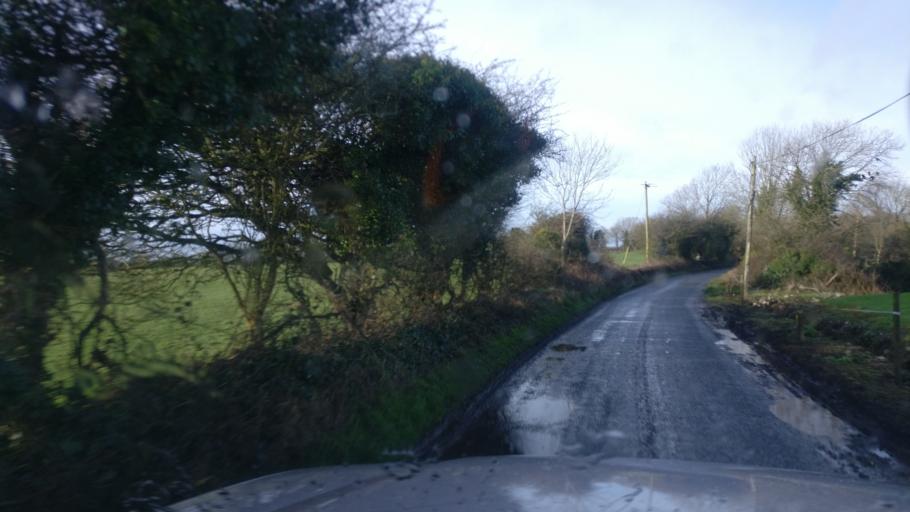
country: IE
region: Connaught
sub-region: County Galway
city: Loughrea
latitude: 53.1994
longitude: -8.6583
